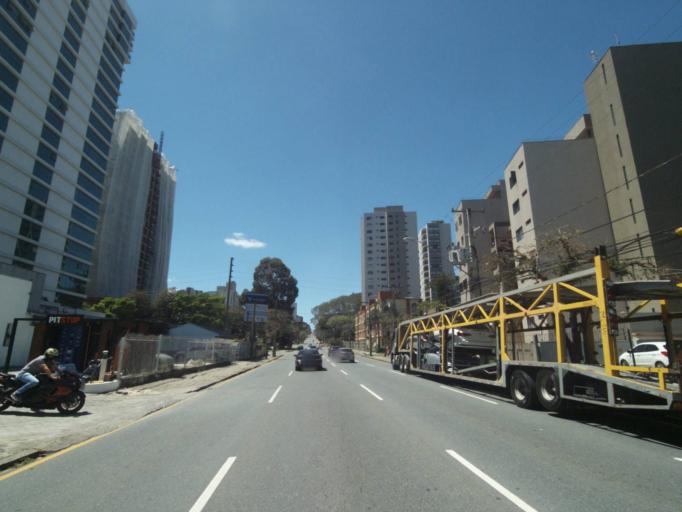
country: BR
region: Parana
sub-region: Curitiba
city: Curitiba
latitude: -25.4064
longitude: -49.2511
